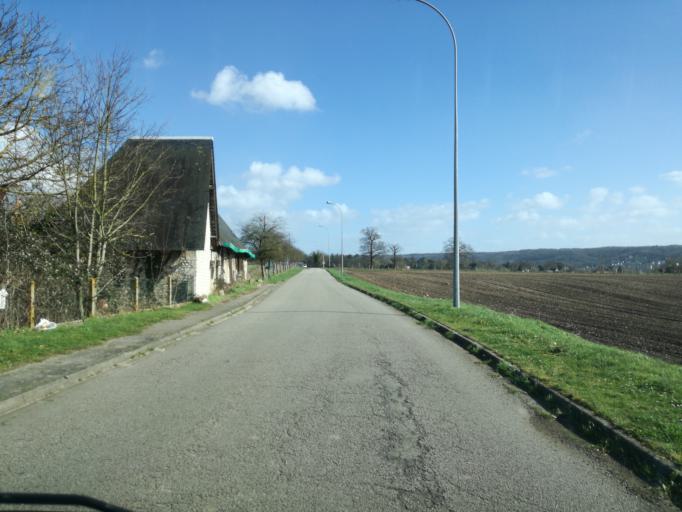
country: FR
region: Haute-Normandie
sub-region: Departement de la Seine-Maritime
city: Sahurs
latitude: 49.3582
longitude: 0.9459
